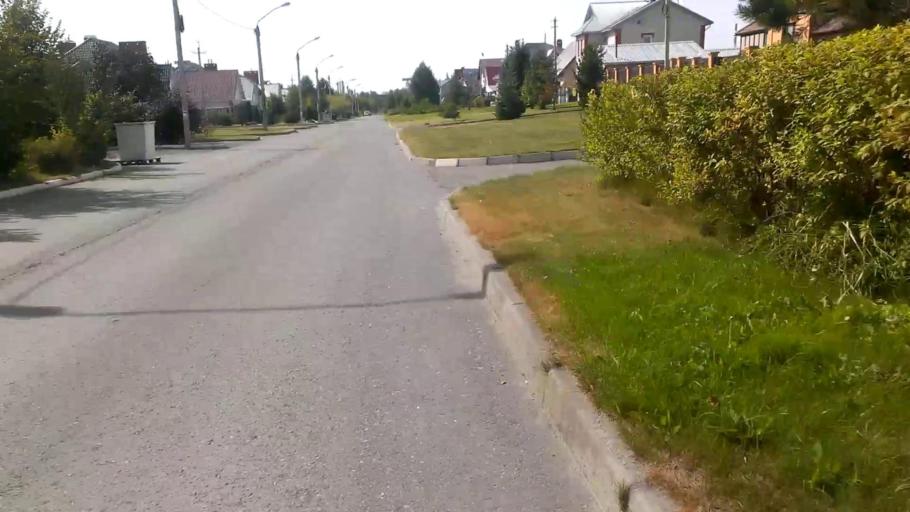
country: RU
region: Altai Krai
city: Novosilikatnyy
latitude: 53.3546
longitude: 83.6525
